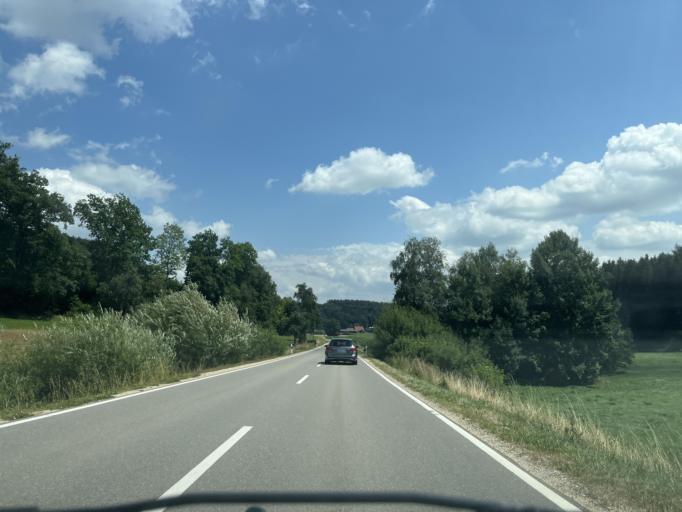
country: DE
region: Baden-Wuerttemberg
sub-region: Tuebingen Region
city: Krauchenwies
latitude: 47.9804
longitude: 9.2196
